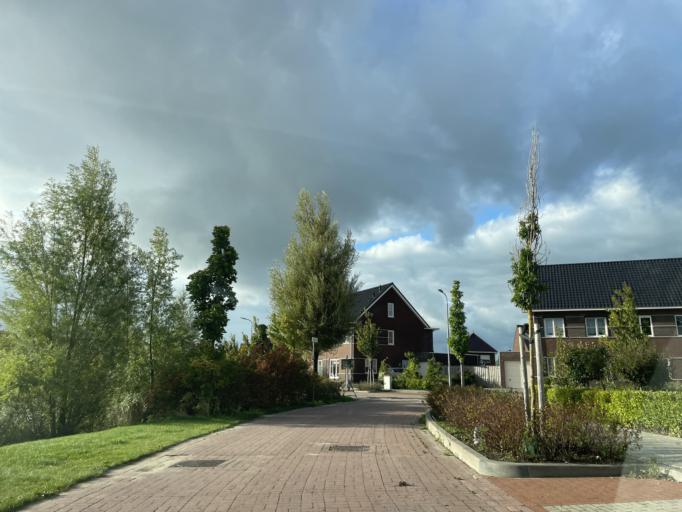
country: NL
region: Zeeland
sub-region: Gemeente Veere
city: Veere
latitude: 51.5090
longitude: 3.6710
